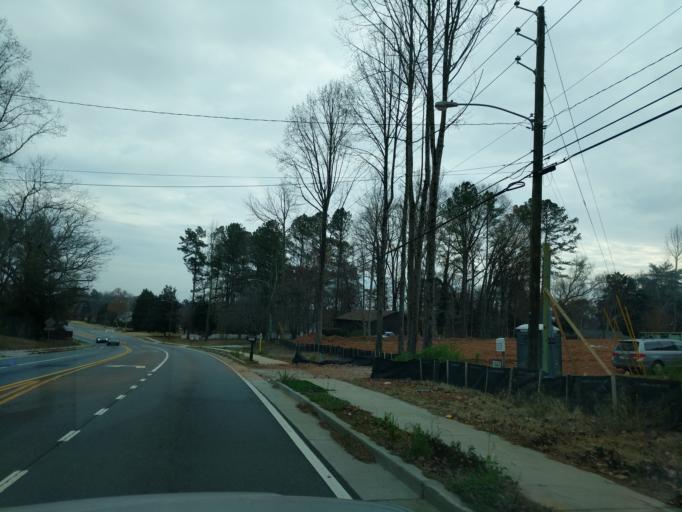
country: US
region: Georgia
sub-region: Gwinnett County
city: Duluth
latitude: 33.9825
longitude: -84.1199
